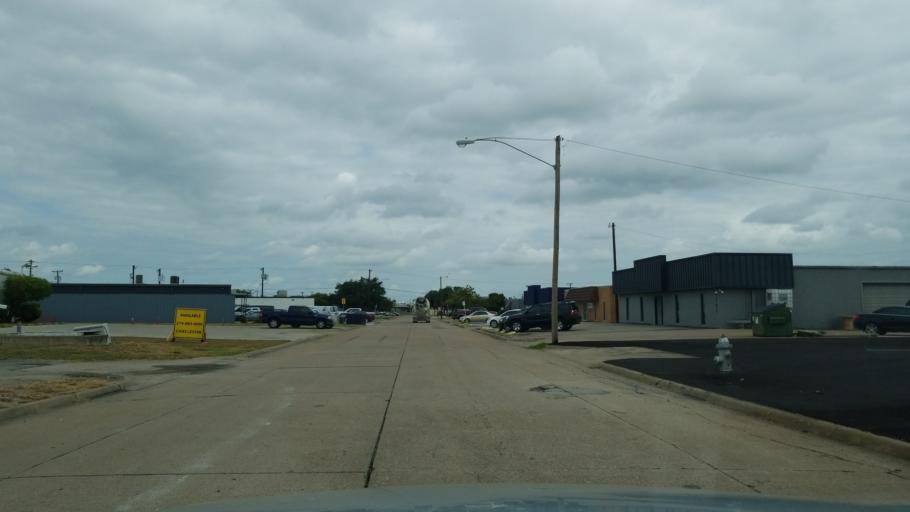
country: US
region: Texas
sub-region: Dallas County
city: Garland
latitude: 32.8834
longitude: -96.6723
